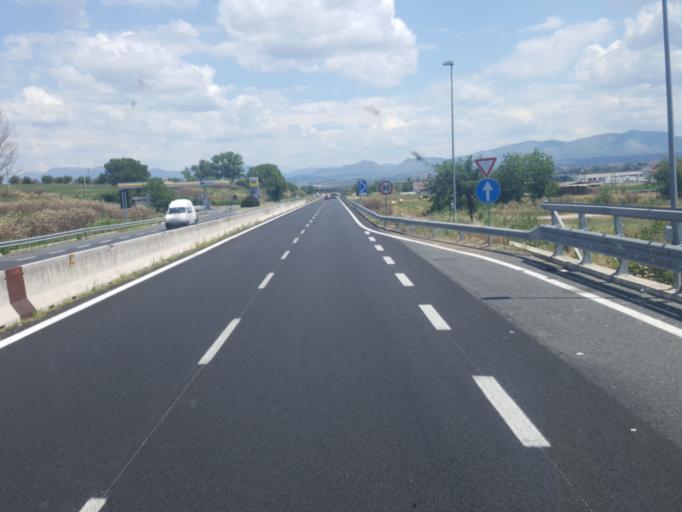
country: IT
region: Latium
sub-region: Citta metropolitana di Roma Capitale
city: Fiano Romano
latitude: 42.1427
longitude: 12.6133
